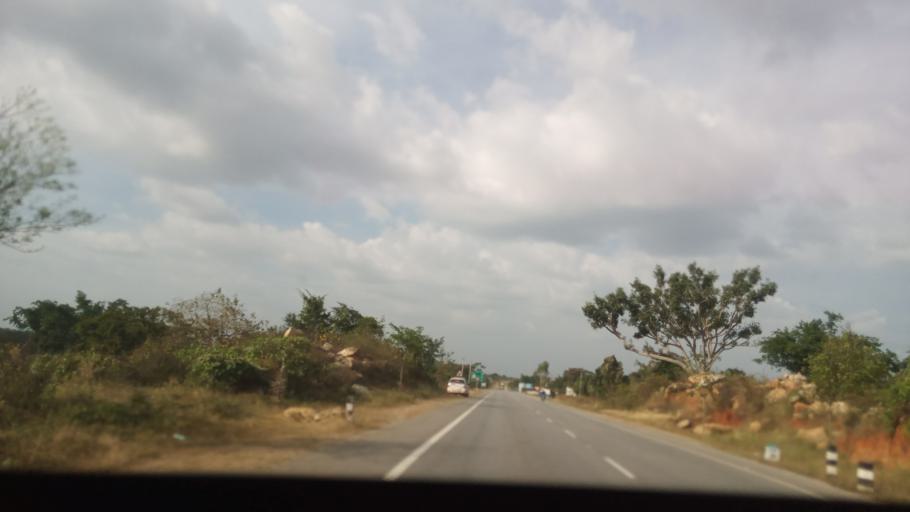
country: IN
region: Karnataka
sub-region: Tumkur
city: Kunigal
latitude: 12.8237
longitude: 77.0274
